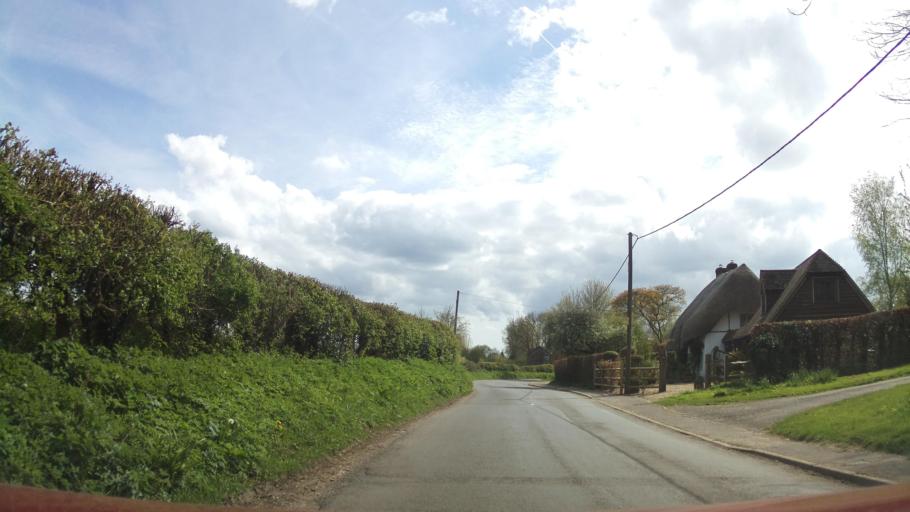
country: GB
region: England
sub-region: Hampshire
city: Romsey
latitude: 51.0903
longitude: -1.5117
